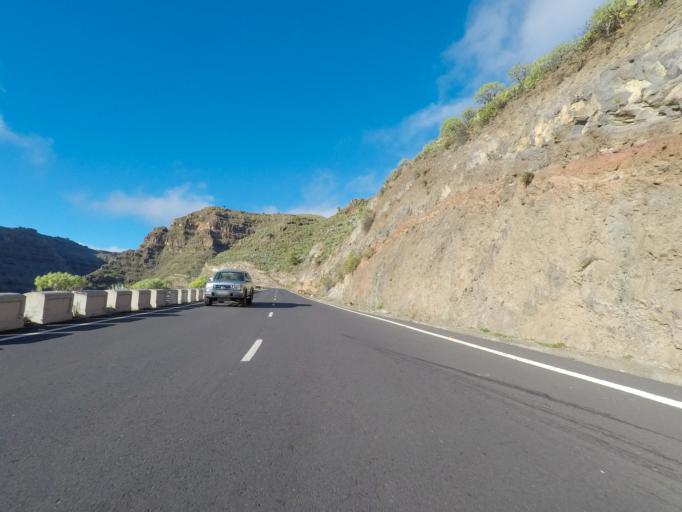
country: ES
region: Canary Islands
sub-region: Provincia de Santa Cruz de Tenerife
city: Vallehermosa
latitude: 28.1161
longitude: -17.3204
